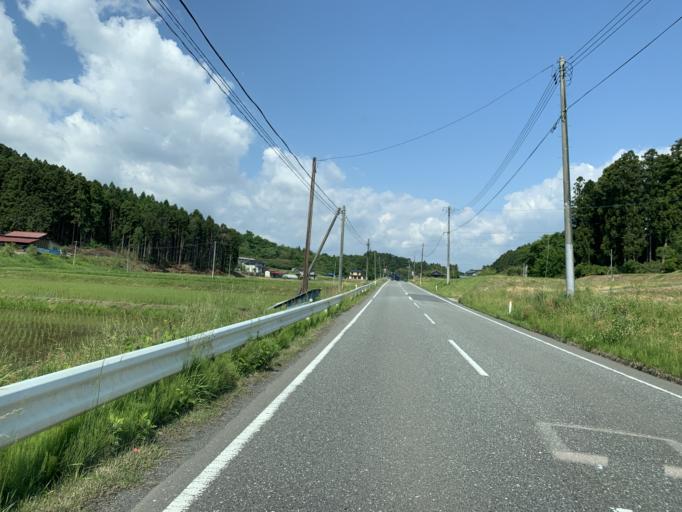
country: JP
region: Iwate
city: Ichinoseki
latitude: 38.7953
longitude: 141.0369
